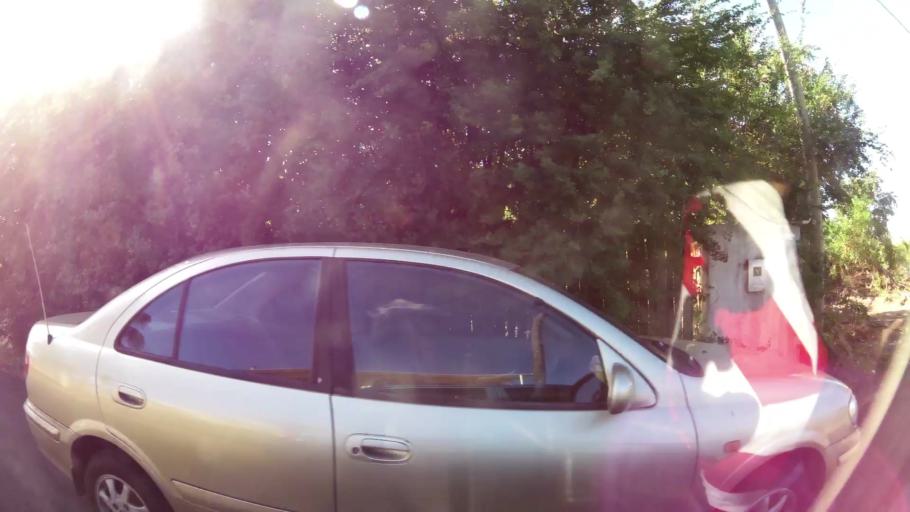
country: MU
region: Black River
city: Albion
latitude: -20.2077
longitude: 57.4066
